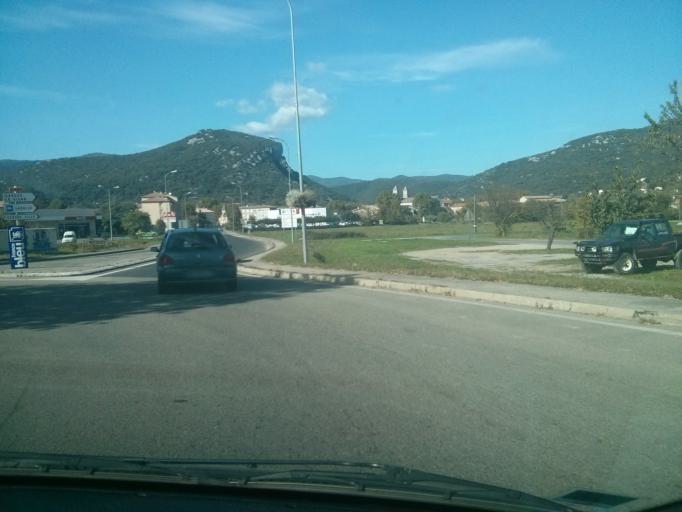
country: FR
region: Languedoc-Roussillon
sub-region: Departement du Gard
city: Saint-Hippolyte-du-Fort
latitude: 43.9583
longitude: 3.8612
